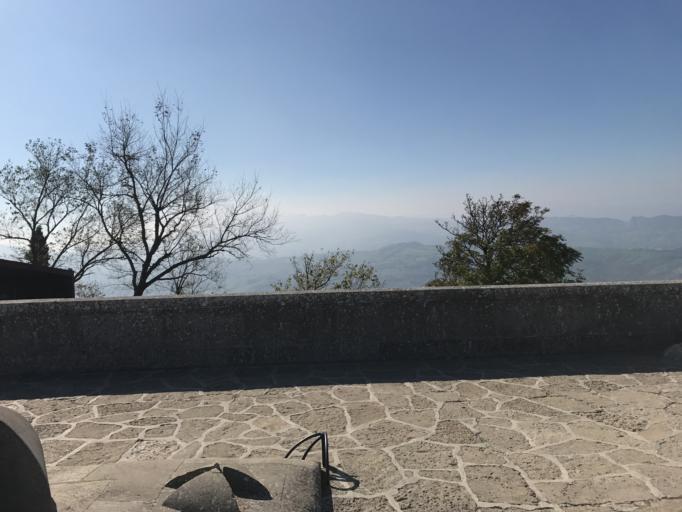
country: SM
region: San Marino
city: San Marino
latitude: 43.9357
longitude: 12.4489
